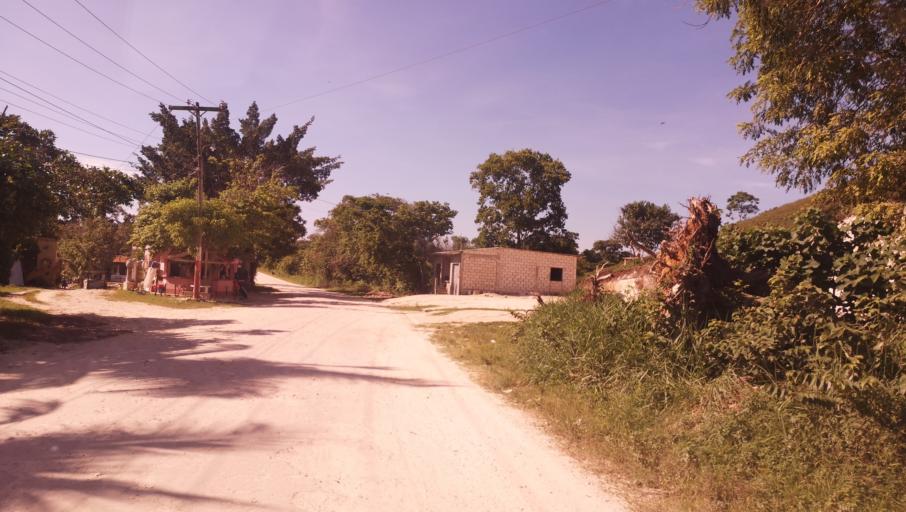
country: GT
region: Peten
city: Dolores
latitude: 16.7236
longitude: -89.3784
